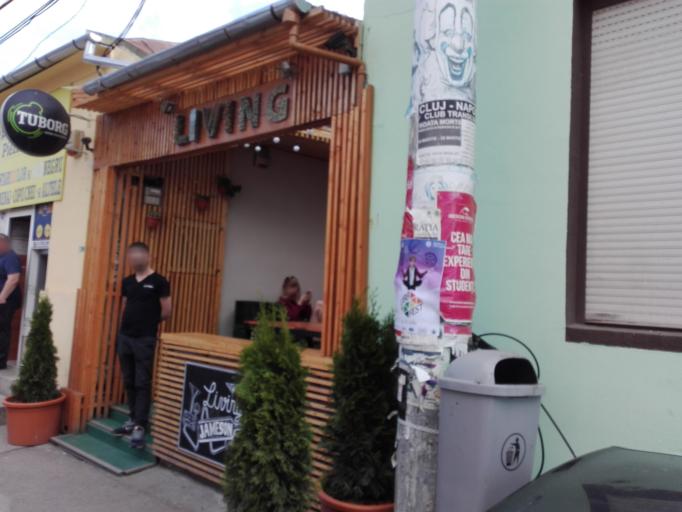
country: RO
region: Cluj
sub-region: Municipiul Cluj-Napoca
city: Cluj-Napoca
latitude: 46.7637
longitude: 23.5771
